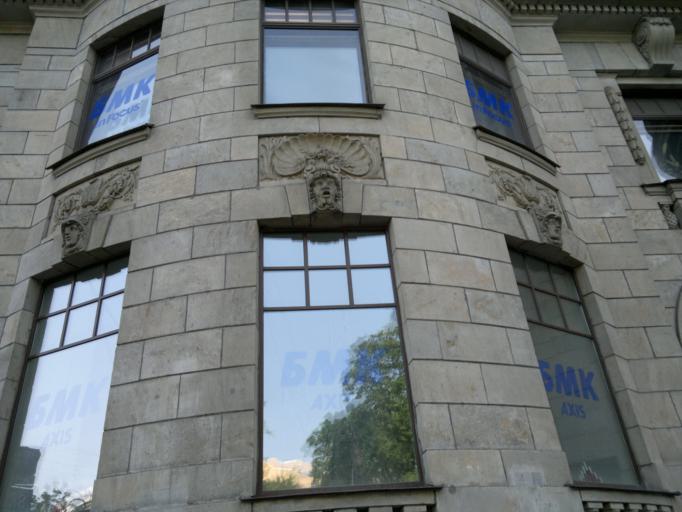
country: RU
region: St.-Petersburg
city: Petrogradka
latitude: 59.9620
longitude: 30.3151
